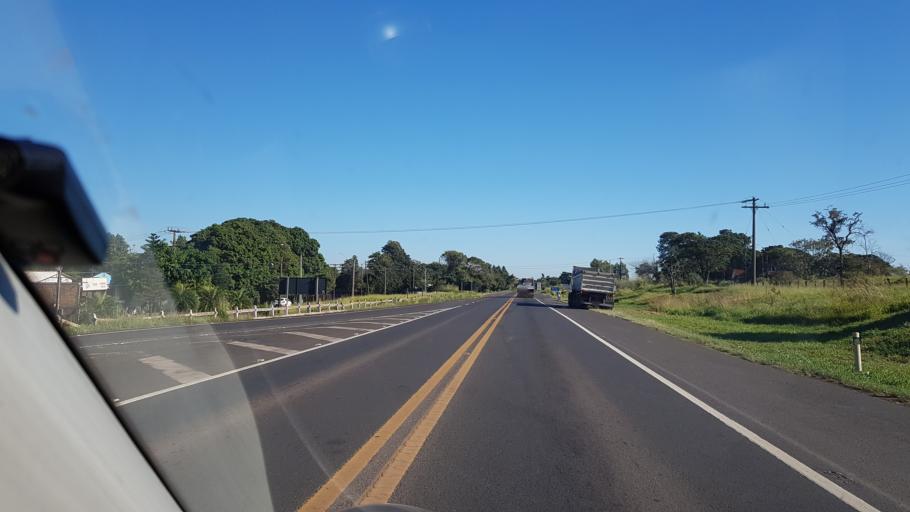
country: BR
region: Sao Paulo
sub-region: Assis
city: Assis
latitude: -22.6337
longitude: -50.4365
